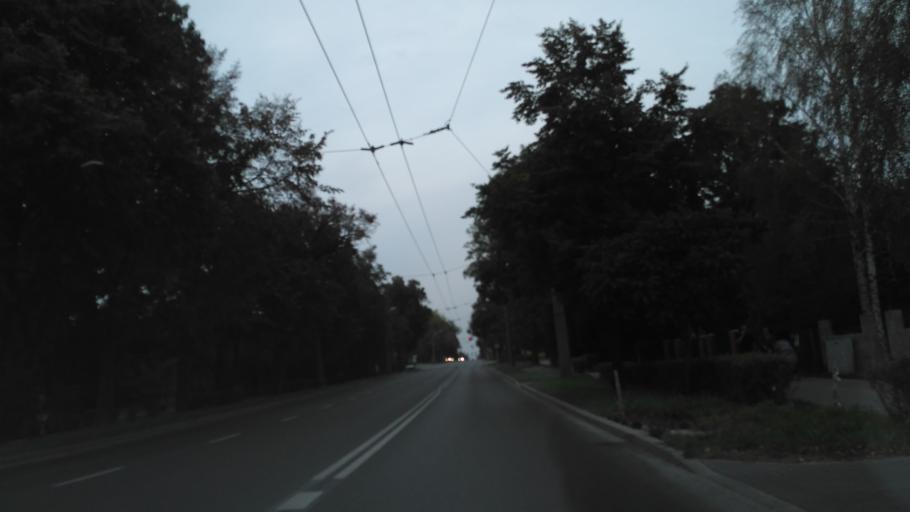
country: PL
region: Lublin Voivodeship
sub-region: Powiat lubelski
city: Lublin
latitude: 51.2284
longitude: 22.5996
